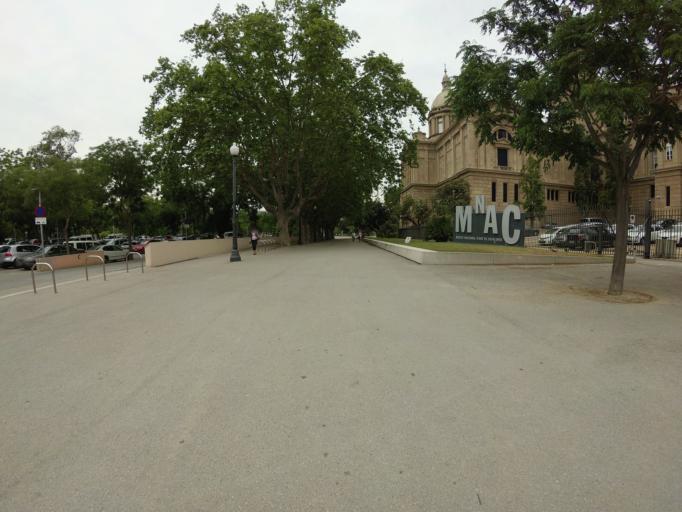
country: ES
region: Catalonia
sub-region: Provincia de Barcelona
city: Sants-Montjuic
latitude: 41.3676
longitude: 2.1528
